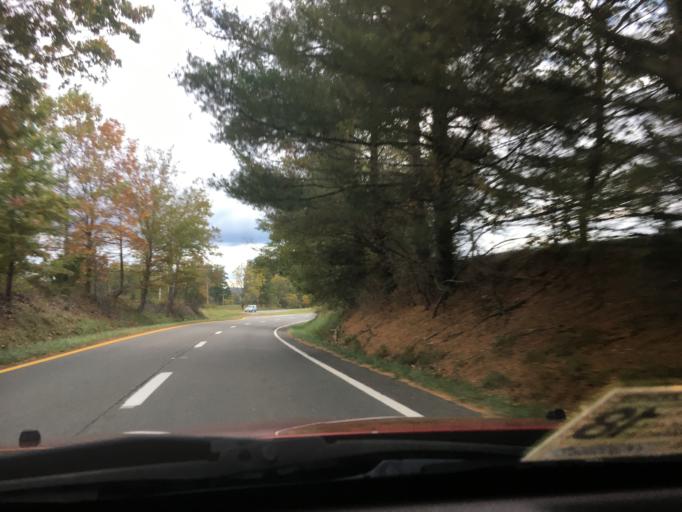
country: US
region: Virginia
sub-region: Pulaski County
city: Dublin
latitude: 37.1549
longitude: -80.6937
